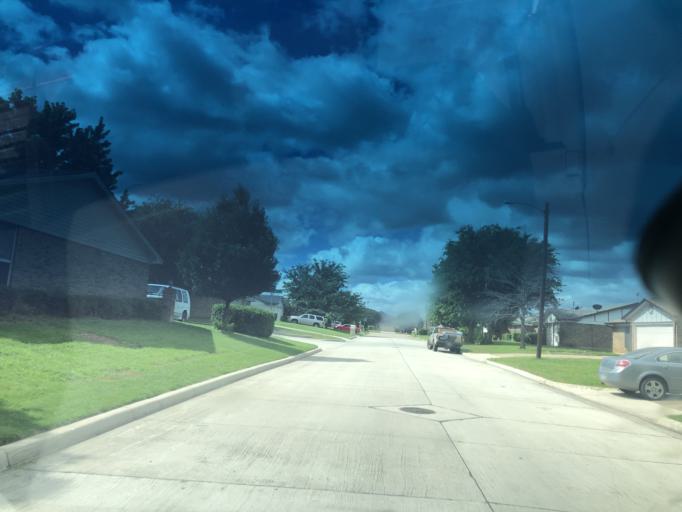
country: US
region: Texas
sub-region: Dallas County
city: Grand Prairie
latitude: 32.7075
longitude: -97.0416
